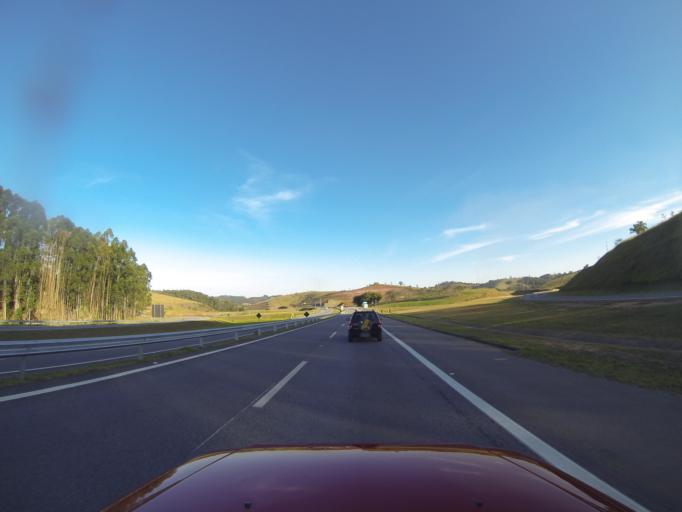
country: BR
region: Sao Paulo
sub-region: Jacarei
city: Jacarei
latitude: -23.3418
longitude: -46.0228
